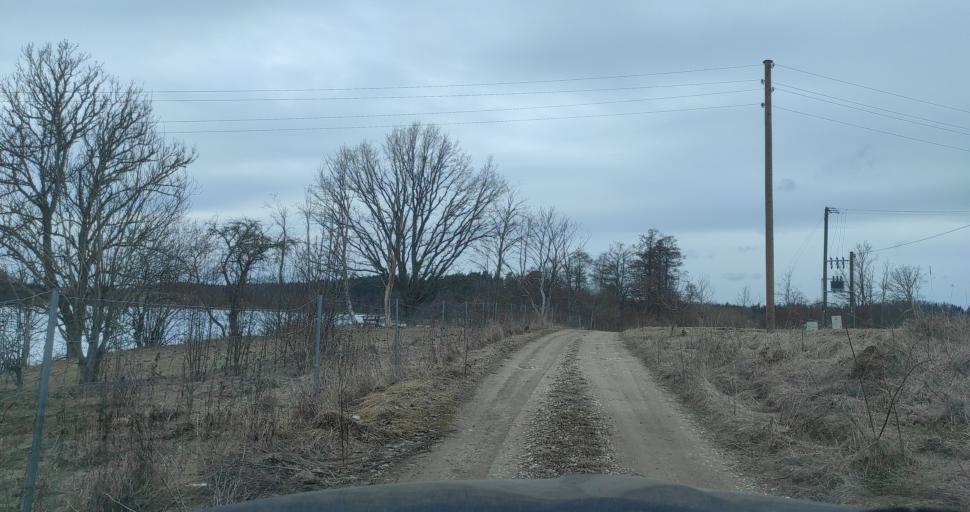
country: LV
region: Tukuma Rajons
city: Tukums
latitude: 57.0970
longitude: 23.0924
